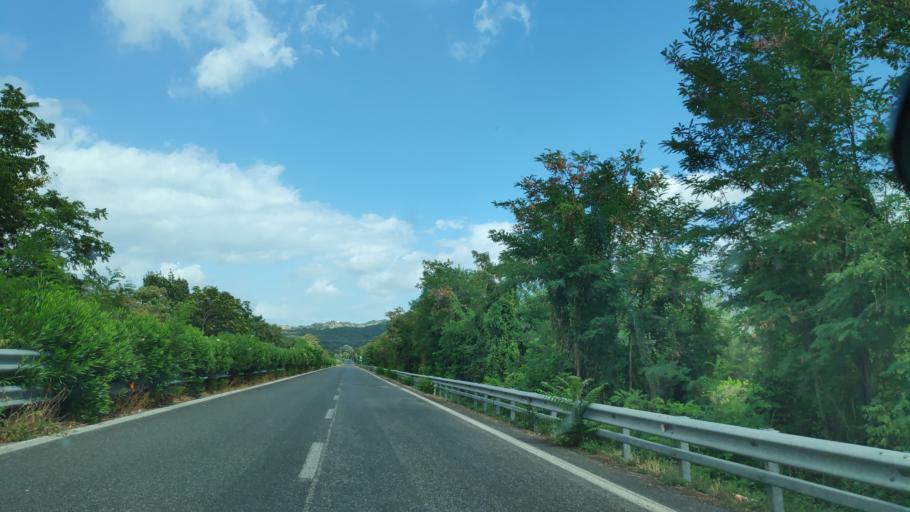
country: IT
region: Campania
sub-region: Provincia di Salerno
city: Serre
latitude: 40.6168
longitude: 15.1674
